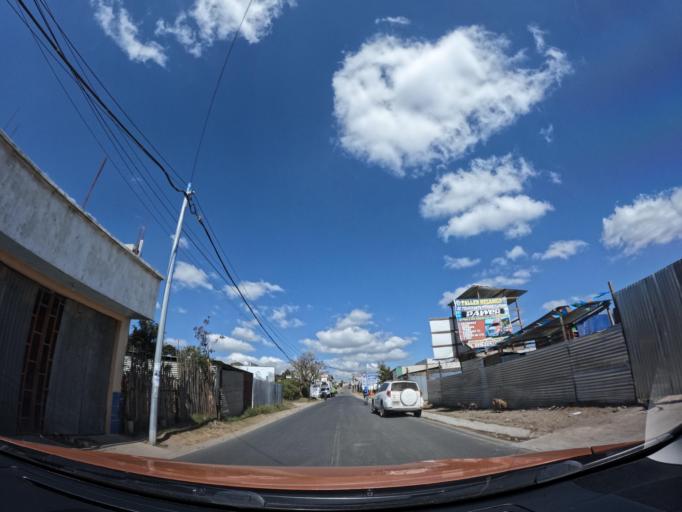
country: GT
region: Chimaltenango
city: Patzun
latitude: 14.6688
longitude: -91.0115
